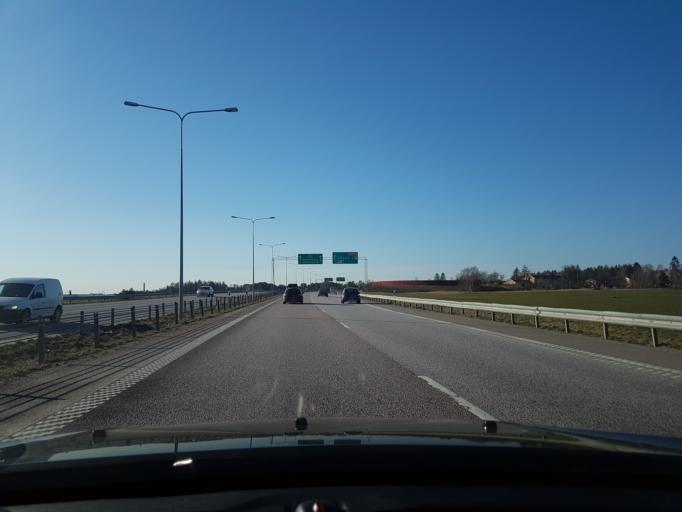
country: SE
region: Uppsala
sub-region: Uppsala Kommun
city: Saevja
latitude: 59.8275
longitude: 17.7404
